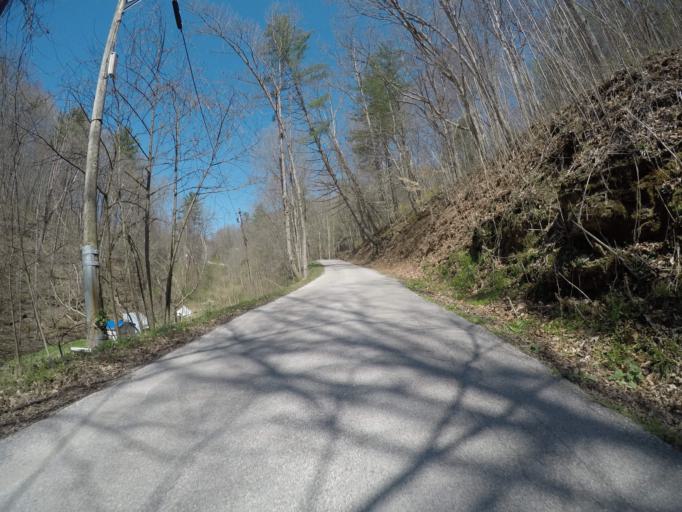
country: US
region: West Virginia
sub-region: Kanawha County
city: Charleston
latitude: 38.4055
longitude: -81.5893
